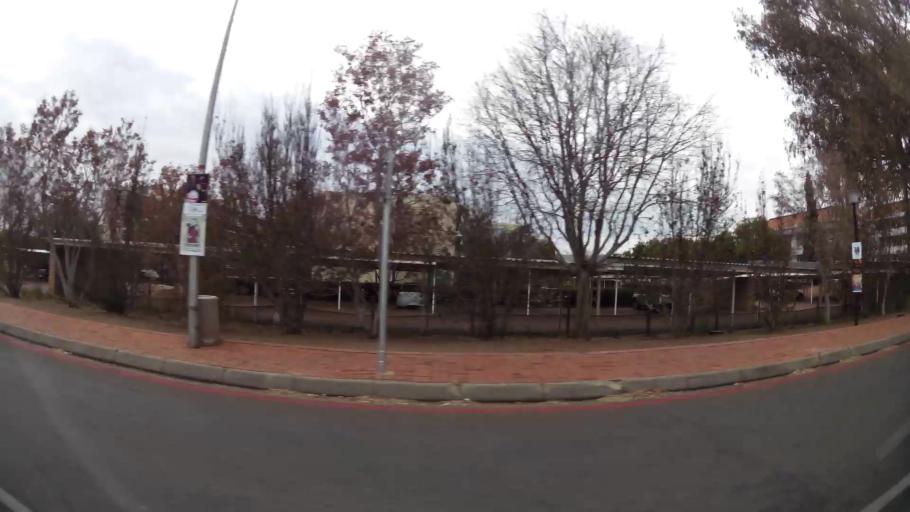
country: ZA
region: Orange Free State
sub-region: Mangaung Metropolitan Municipality
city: Bloemfontein
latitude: -29.1089
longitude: 26.1863
